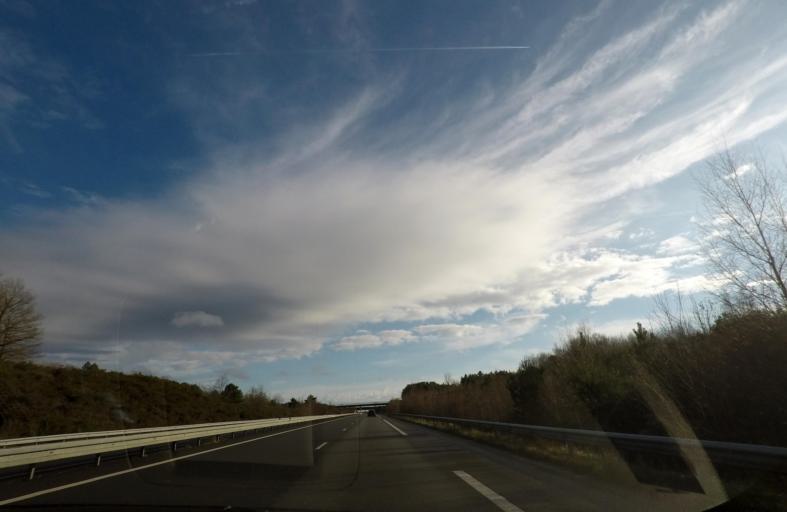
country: FR
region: Centre
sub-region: Departement du Loir-et-Cher
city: Villefranche-sur-Cher
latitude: 47.3125
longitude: 1.8233
